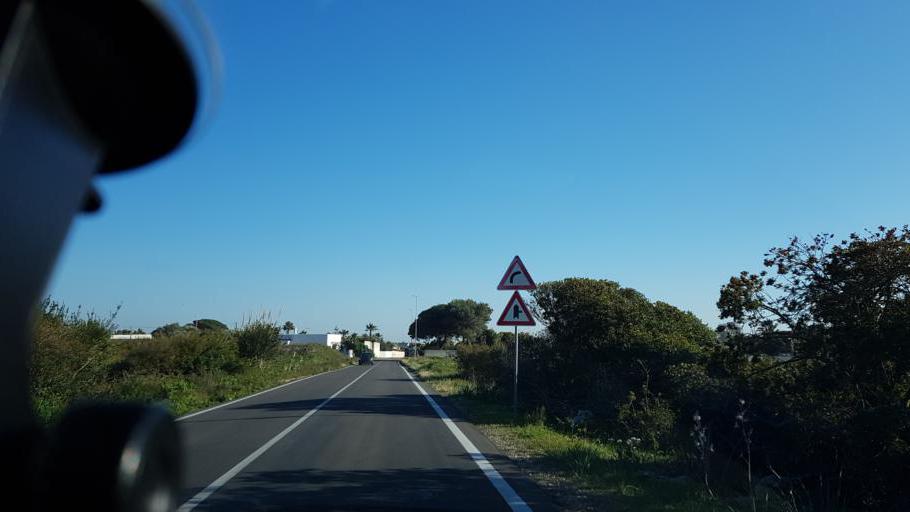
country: IT
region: Apulia
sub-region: Provincia di Lecce
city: Merine
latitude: 40.4327
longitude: 18.2412
